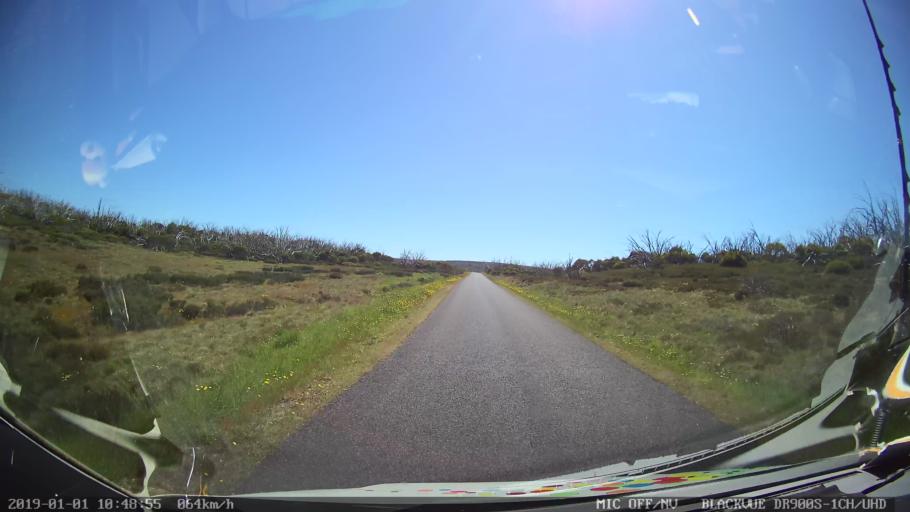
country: AU
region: New South Wales
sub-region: Snowy River
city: Jindabyne
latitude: -36.0374
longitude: 148.3656
